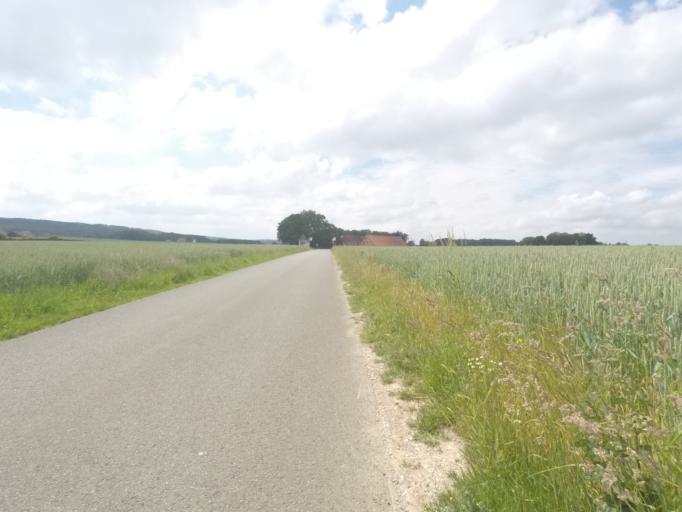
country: DE
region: North Rhine-Westphalia
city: Borgholzhausen
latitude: 52.1398
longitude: 8.3327
